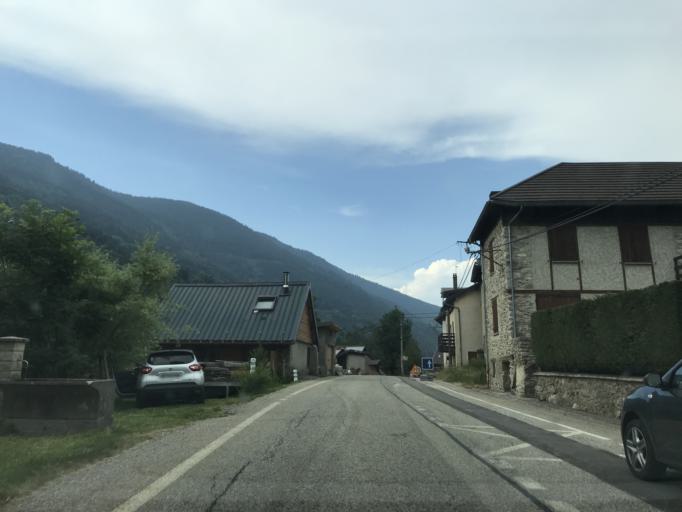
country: FR
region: Rhone-Alpes
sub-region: Departement de l'Isere
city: Theys
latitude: 45.3059
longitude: 6.0798
